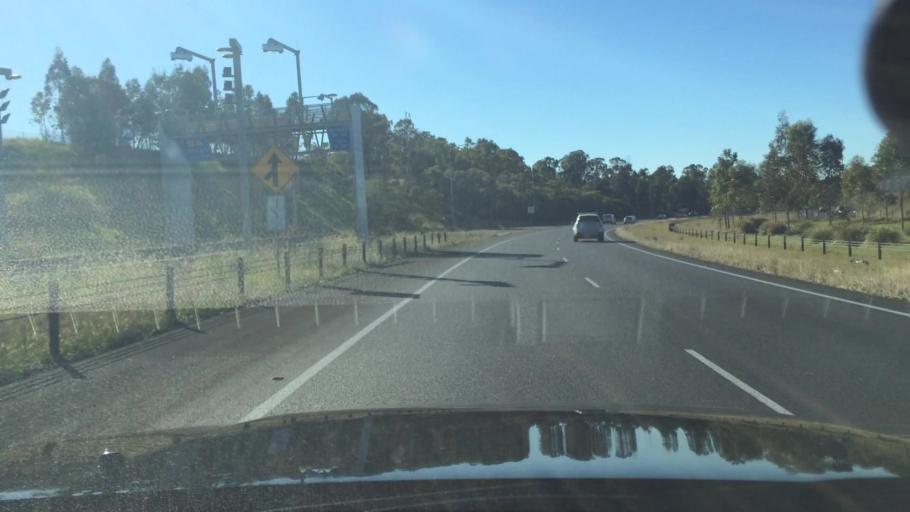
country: AU
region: New South Wales
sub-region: Blacktown
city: Hassall Grove
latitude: -33.7303
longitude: 150.8524
